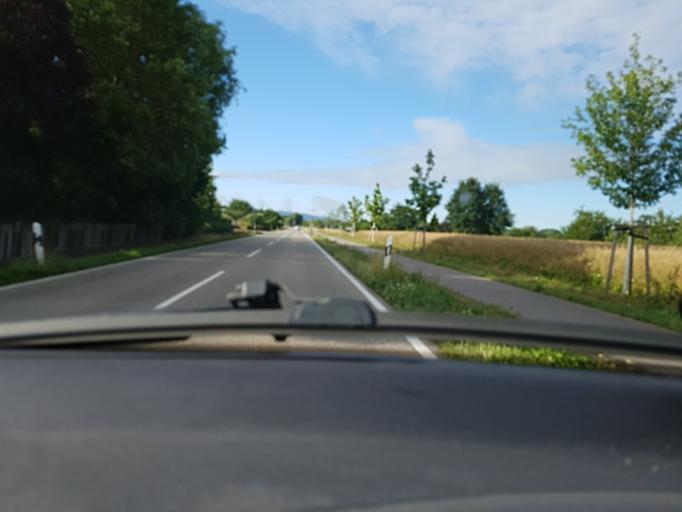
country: DE
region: Baden-Wuerttemberg
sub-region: Freiburg Region
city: Offenburg
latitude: 48.4962
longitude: 7.9151
